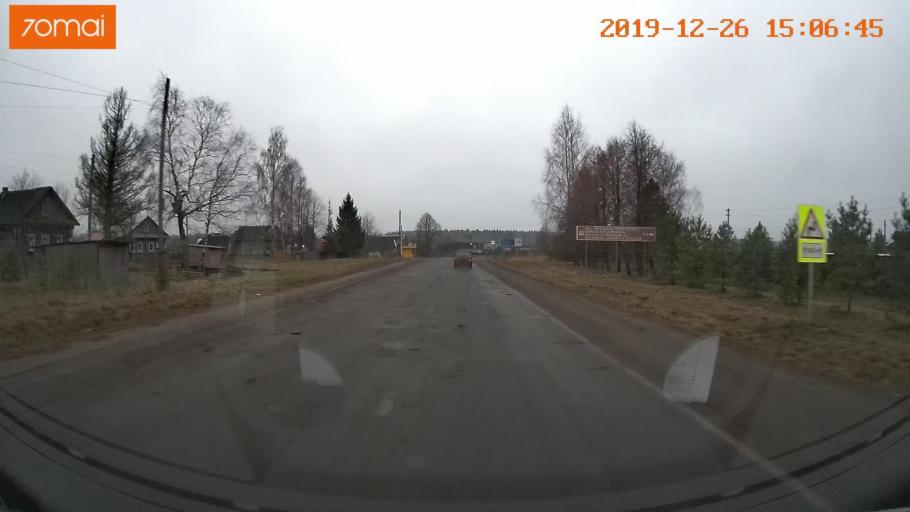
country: RU
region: Jaroslavl
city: Rybinsk
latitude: 58.1754
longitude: 38.8437
